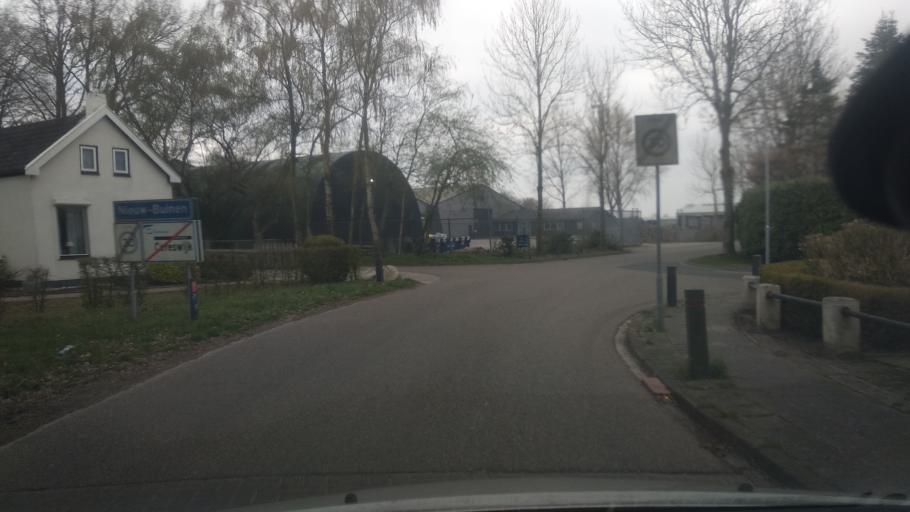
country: NL
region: Groningen
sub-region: Gemeente Stadskanaal
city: Stadskanaal
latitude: 52.9648
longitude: 6.9696
